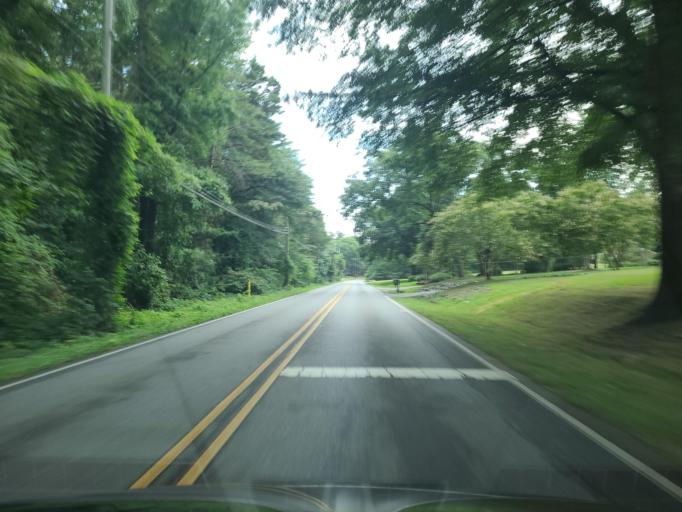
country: US
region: North Carolina
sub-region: Gaston County
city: Dallas
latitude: 35.2993
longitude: -81.1797
